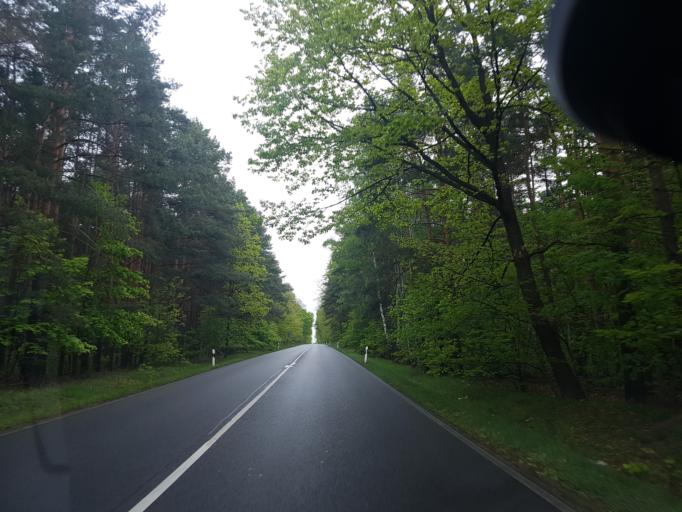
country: DE
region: Brandenburg
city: Neupetershain
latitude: 51.5918
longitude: 14.1148
